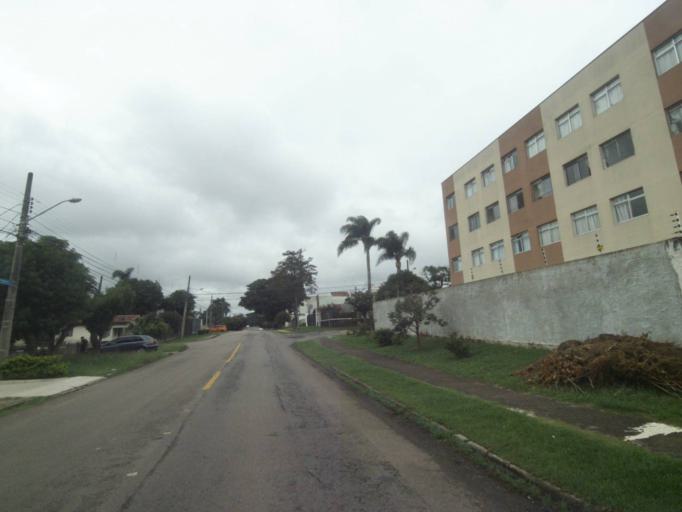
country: BR
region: Parana
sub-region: Curitiba
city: Curitiba
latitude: -25.4903
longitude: -49.2982
